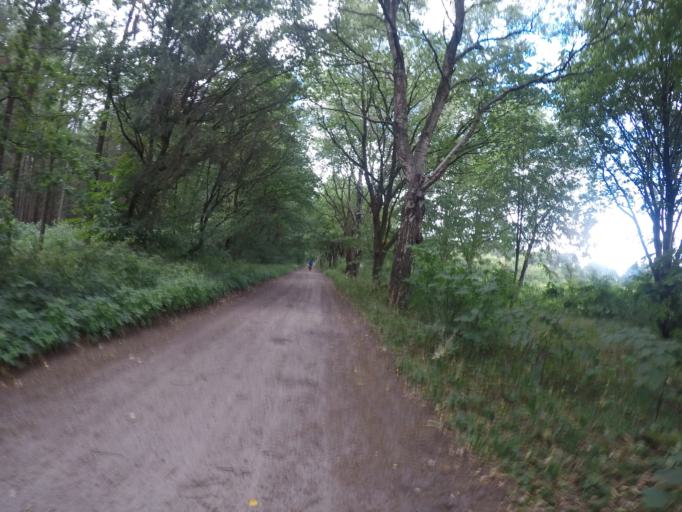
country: DE
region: Lower Saxony
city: Cadenberge
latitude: 53.7497
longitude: 9.0558
